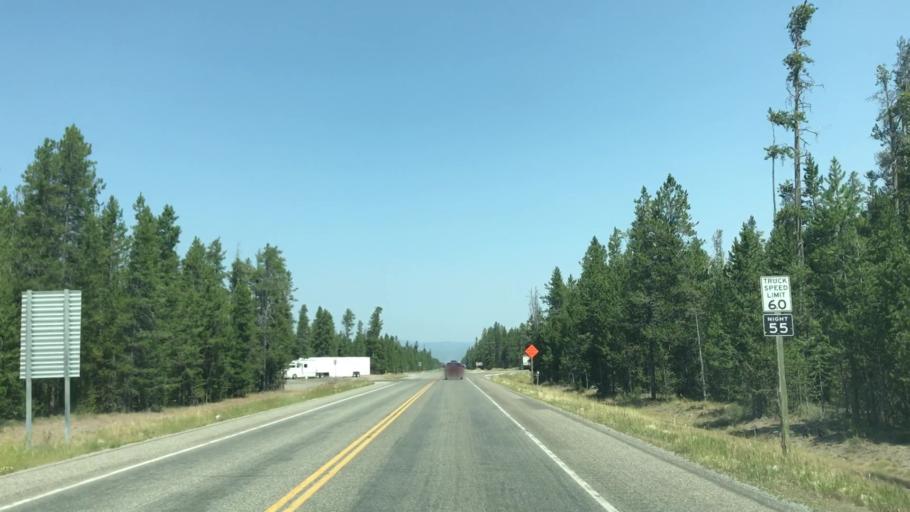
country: US
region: Montana
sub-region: Gallatin County
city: West Yellowstone
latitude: 44.6723
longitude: -111.1002
